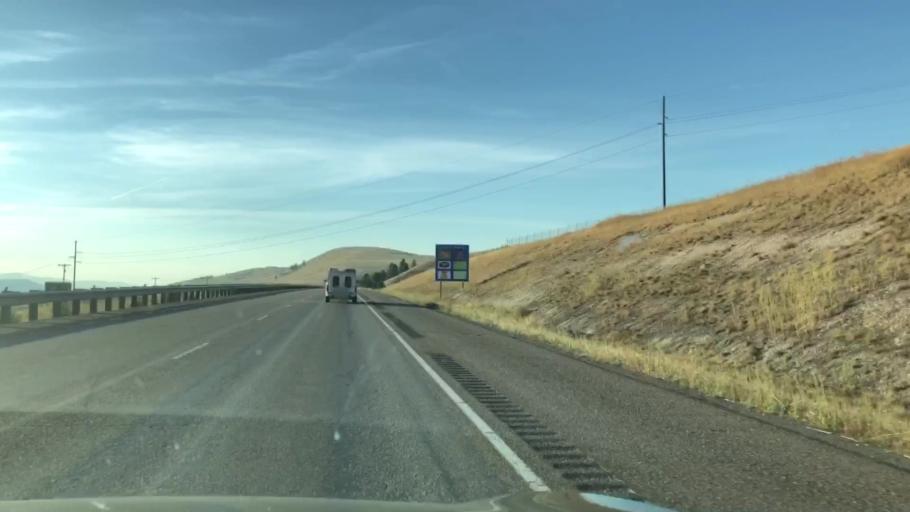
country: US
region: Montana
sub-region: Missoula County
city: Missoula
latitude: 46.9062
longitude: -114.0233
